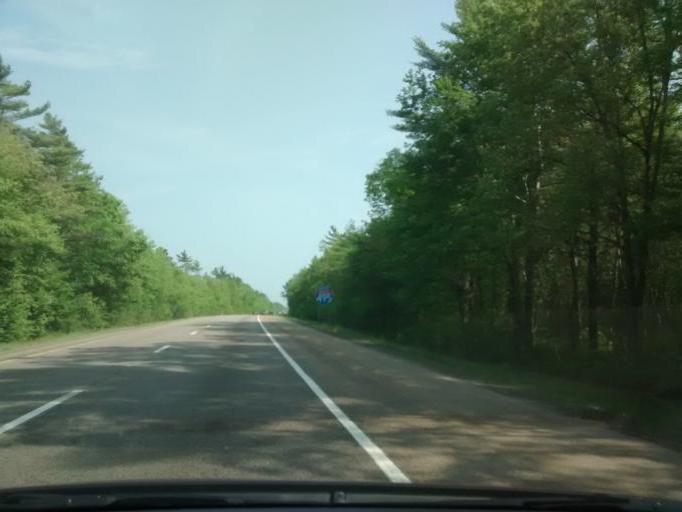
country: US
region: Massachusetts
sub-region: Plymouth County
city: Carver
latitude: 41.8380
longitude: -70.8256
